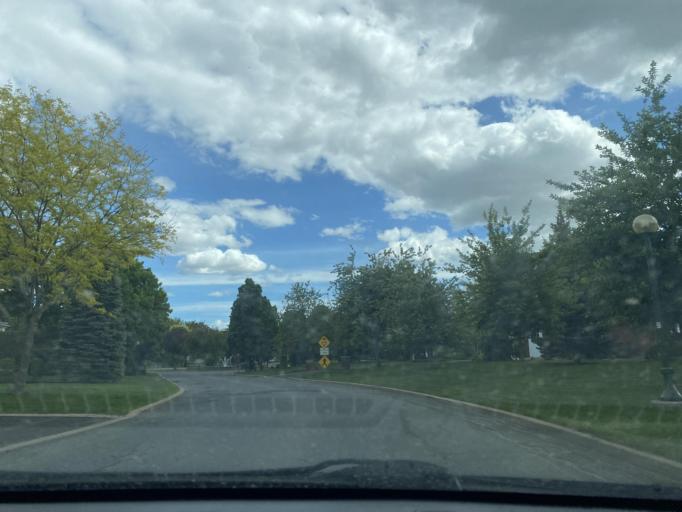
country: CA
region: Quebec
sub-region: Monteregie
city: Carignan
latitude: 45.4680
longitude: -73.2953
